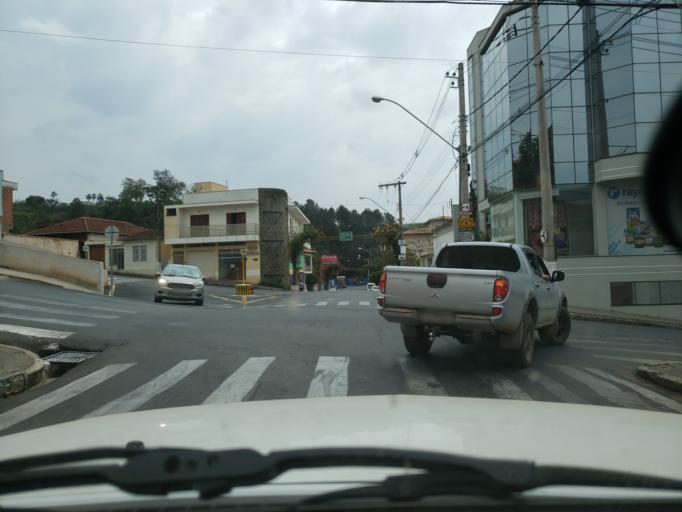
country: BR
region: Minas Gerais
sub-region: Jacutinga
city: Jacutinga
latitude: -22.2835
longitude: -46.6119
